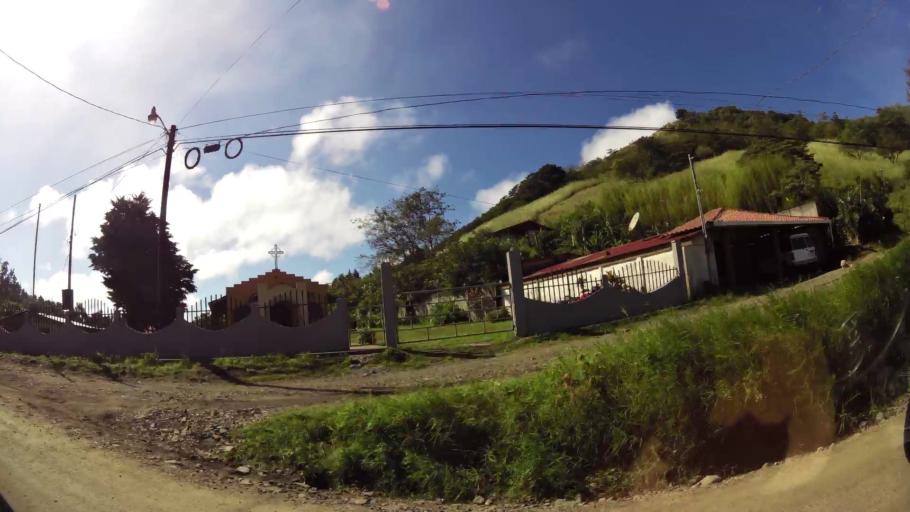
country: CR
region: Guanacaste
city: Juntas
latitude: 10.3288
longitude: -84.8445
